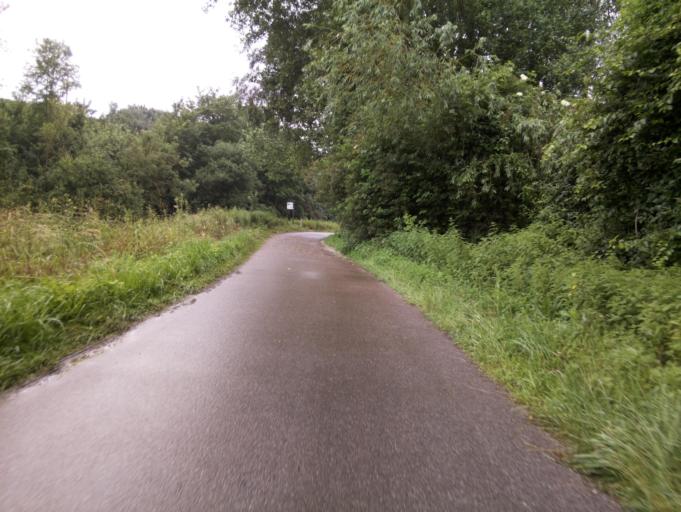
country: FR
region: Picardie
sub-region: Departement de la Somme
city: Dreuil-les-Amiens
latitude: 49.9218
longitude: 2.2146
